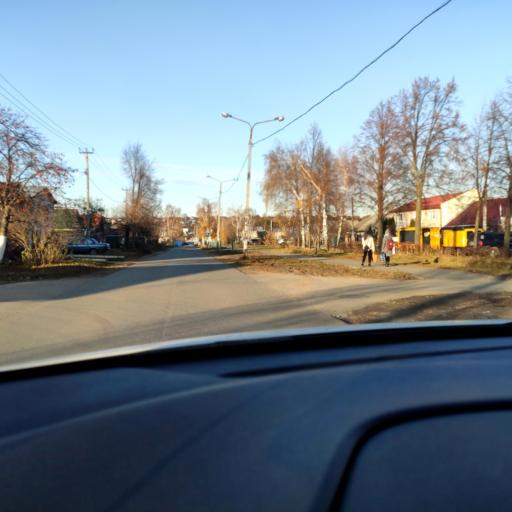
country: RU
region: Tatarstan
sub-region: Gorod Kazan'
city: Kazan
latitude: 55.8796
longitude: 49.0699
